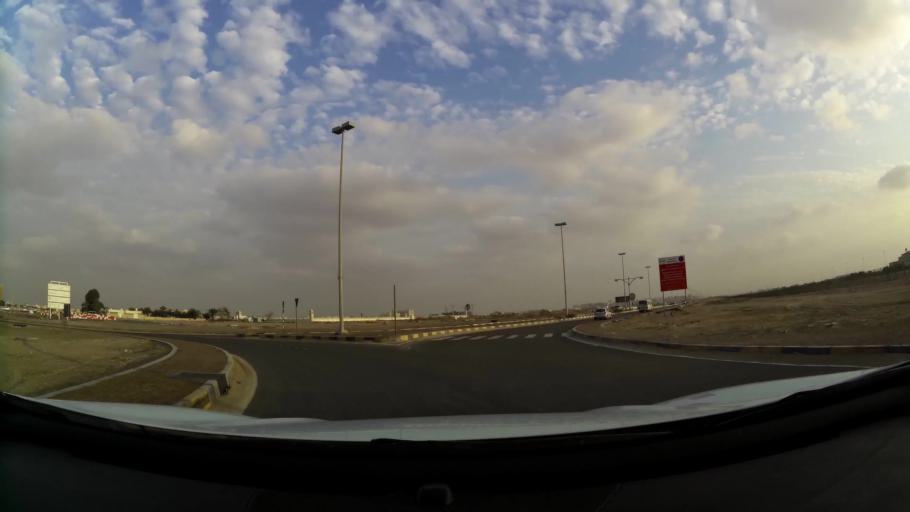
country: AE
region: Abu Dhabi
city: Abu Dhabi
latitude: 24.3691
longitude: 54.5276
